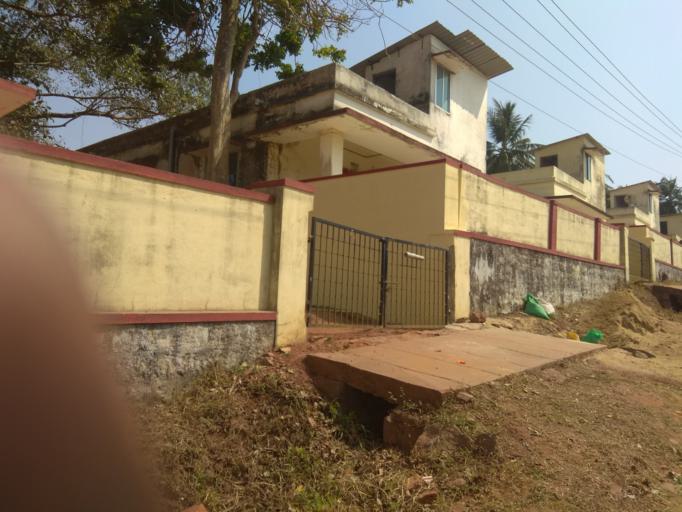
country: IN
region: Karnataka
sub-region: Dakshina Kannada
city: Mangalore
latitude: 12.9407
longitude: 74.8545
